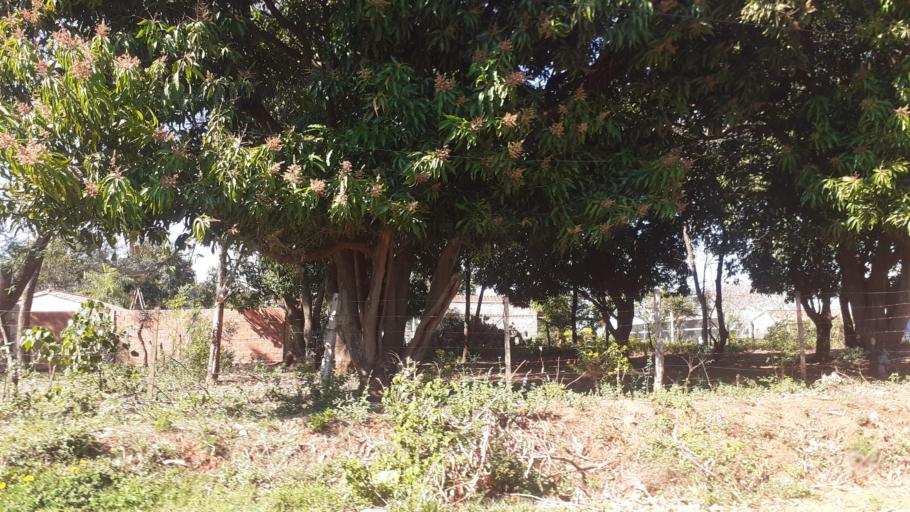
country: PY
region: Misiones
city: San Juan Bautista
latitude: -26.6641
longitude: -57.1250
